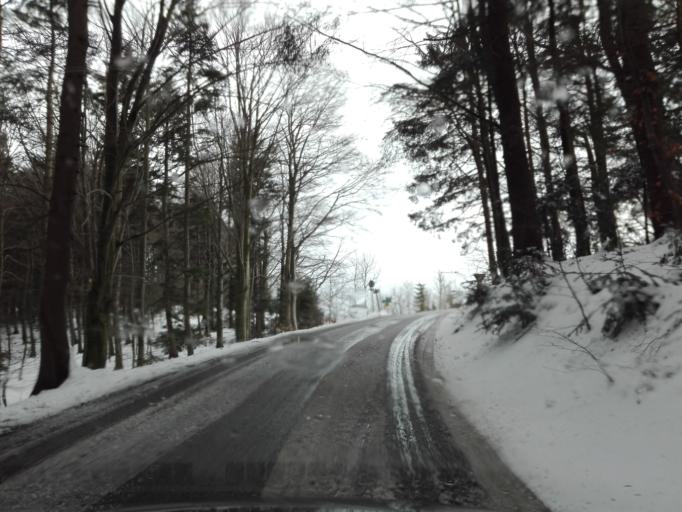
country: AT
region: Upper Austria
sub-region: Politischer Bezirk Rohrbach
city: Pfarrkirchen im Muehlkreis
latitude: 48.5502
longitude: 13.8410
